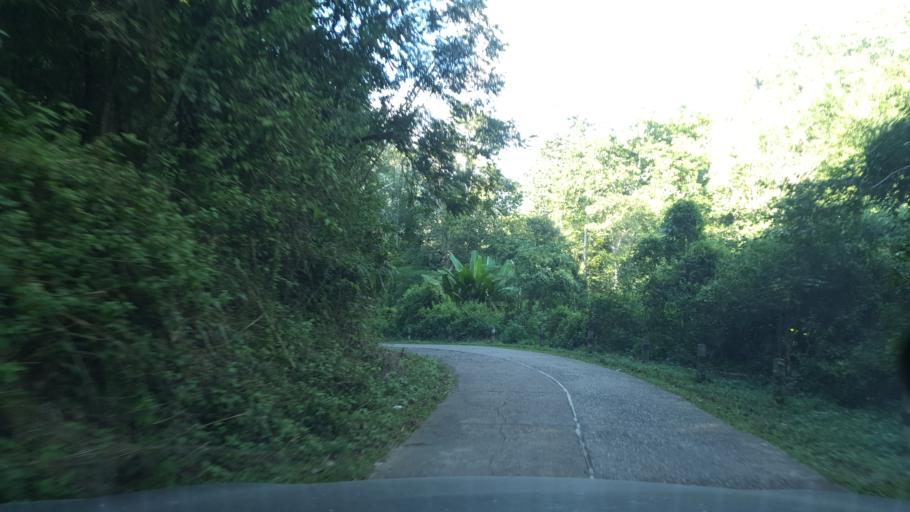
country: TH
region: Chiang Mai
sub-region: Amphoe Chiang Dao
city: Chiang Dao
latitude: 19.3868
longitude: 98.7699
